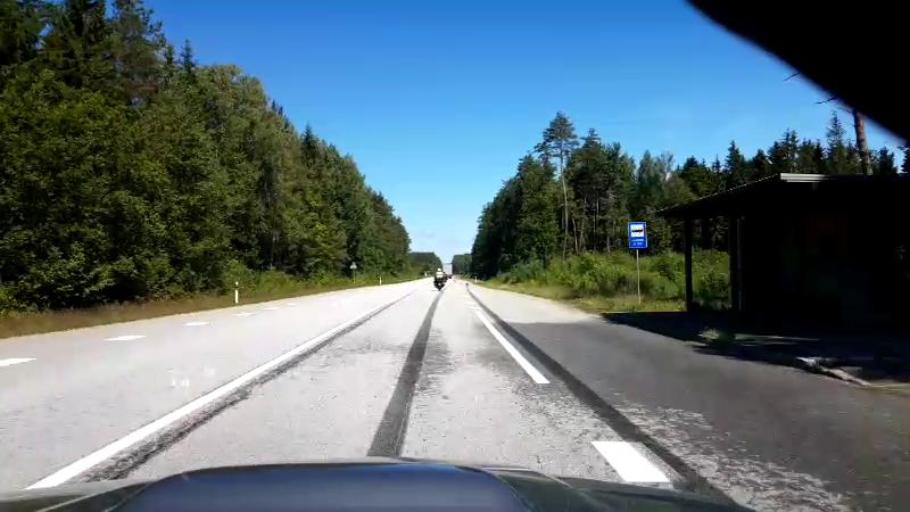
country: LV
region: Saulkrastu
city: Saulkrasti
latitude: 57.4226
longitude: 24.4289
